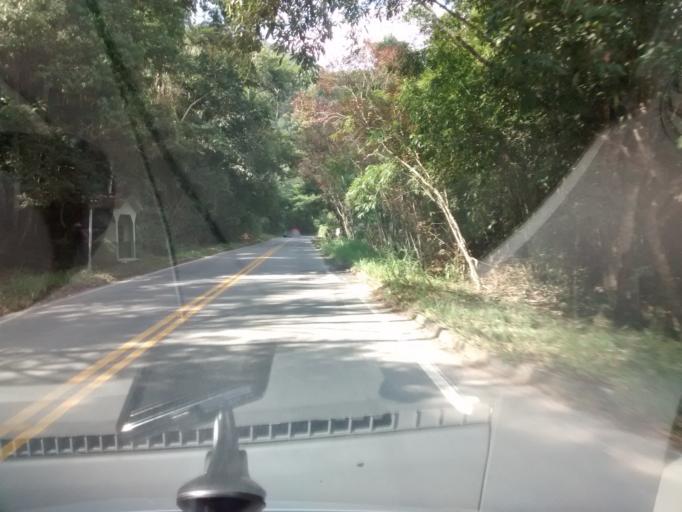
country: BR
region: Rio de Janeiro
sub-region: Miguel Pereira
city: Miguel Pereira
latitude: -22.4717
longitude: -43.5568
